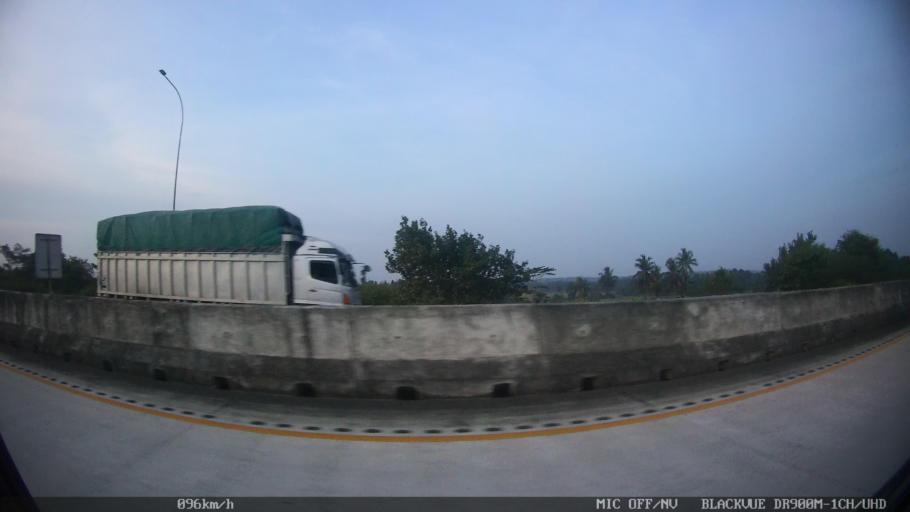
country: ID
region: Lampung
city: Pasuruan
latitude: -5.7303
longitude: 105.6745
